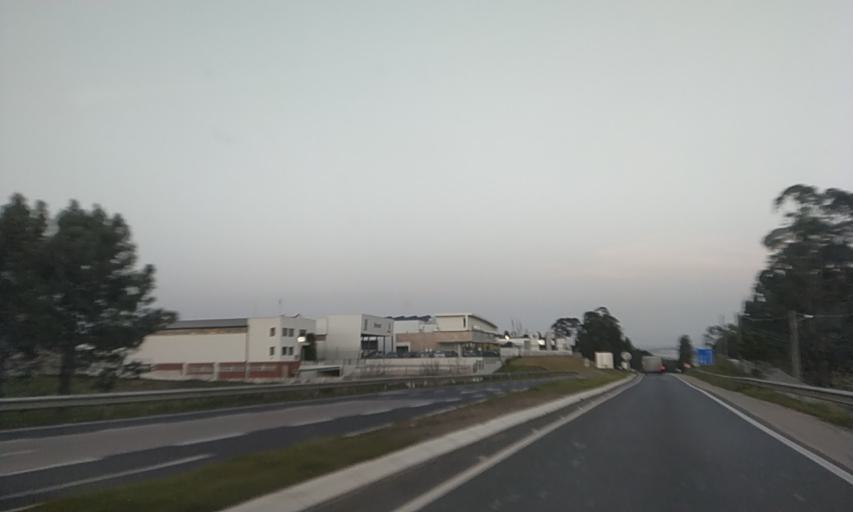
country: PT
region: Leiria
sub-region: Leiria
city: Amor
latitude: 39.7464
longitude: -8.8659
